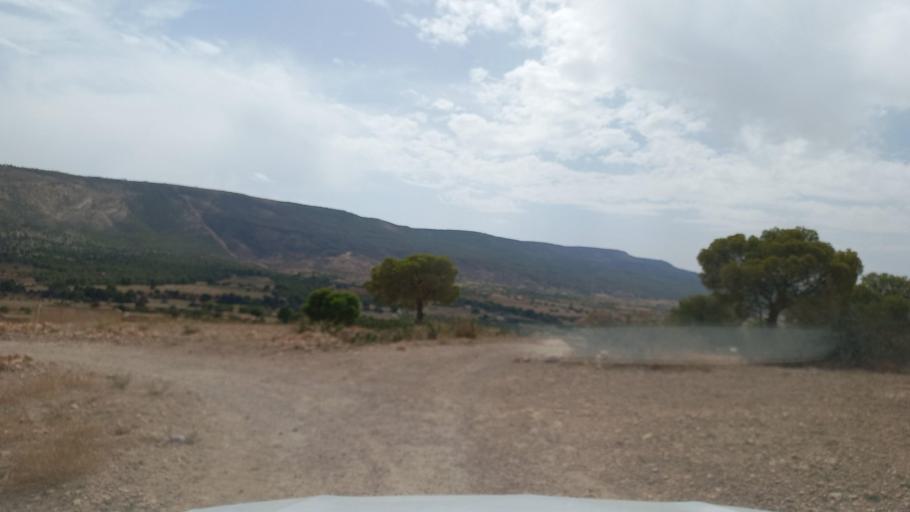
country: TN
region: Al Qasrayn
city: Kasserine
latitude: 35.3733
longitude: 8.9011
